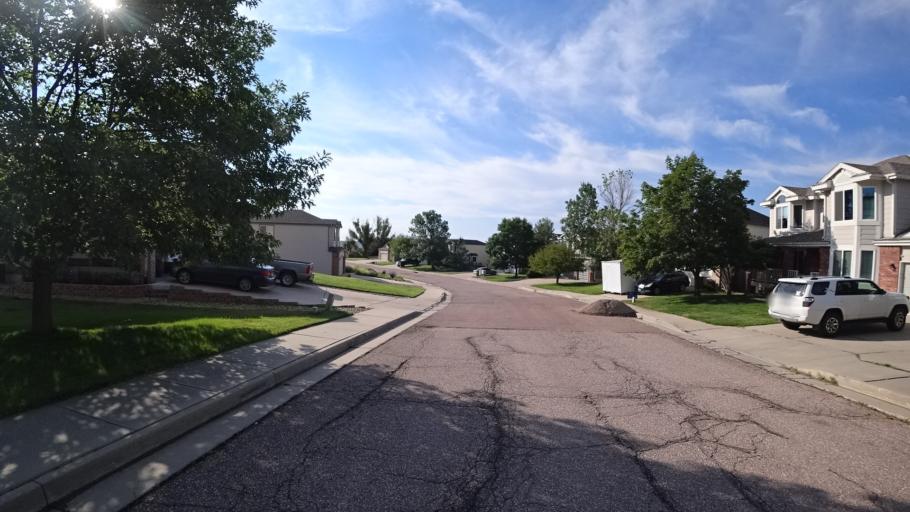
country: US
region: Colorado
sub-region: El Paso County
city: Air Force Academy
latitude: 38.9268
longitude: -104.8577
